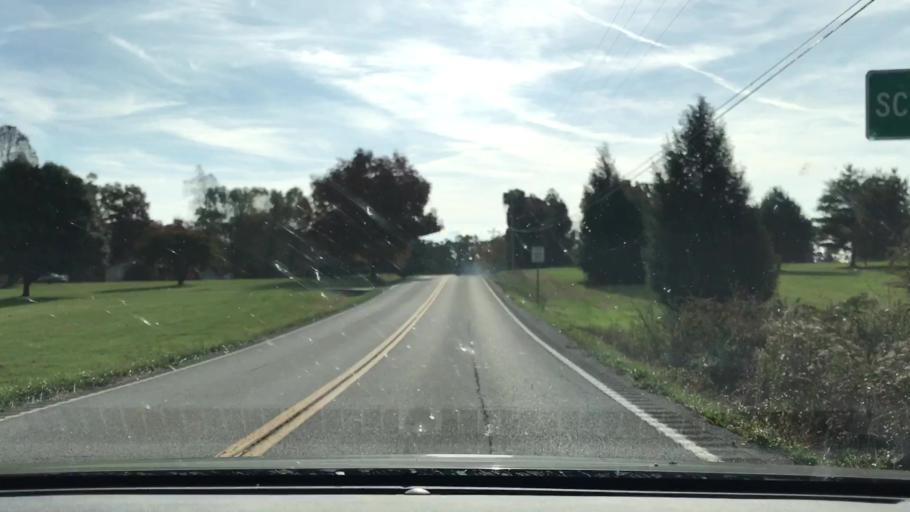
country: US
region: Tennessee
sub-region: Scott County
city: Huntsville
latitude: 36.3482
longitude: -84.6806
